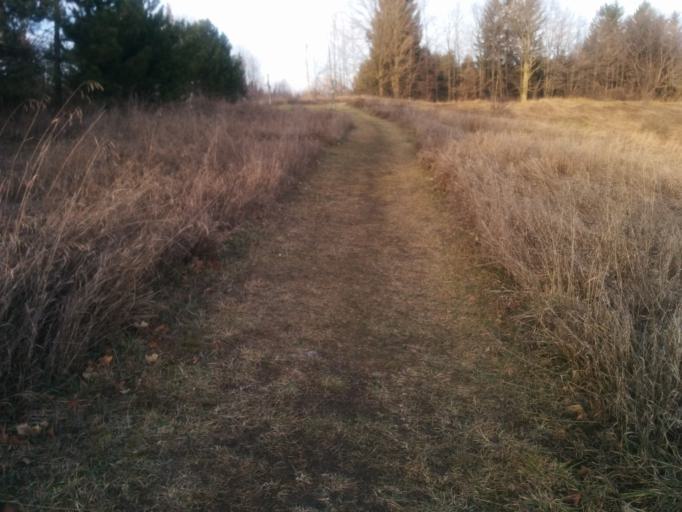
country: CA
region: Ontario
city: Orangeville
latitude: 43.9617
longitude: -79.9795
